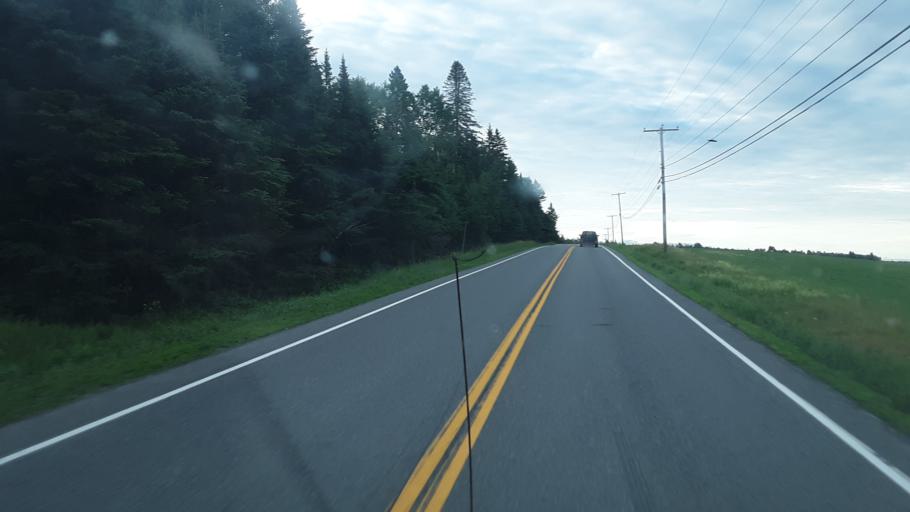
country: US
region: Maine
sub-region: Aroostook County
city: Presque Isle
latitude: 46.5470
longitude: -68.3703
